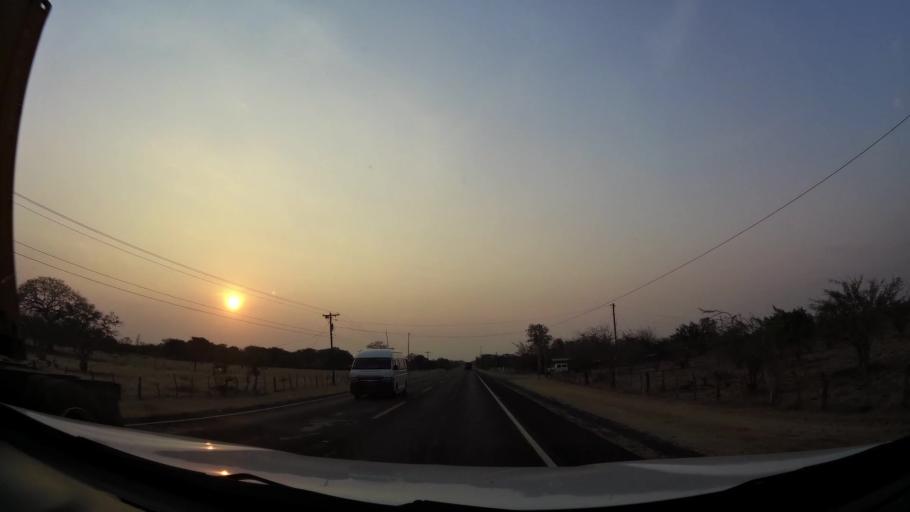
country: NI
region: Leon
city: La Paz Centro
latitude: 12.2878
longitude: -86.7585
